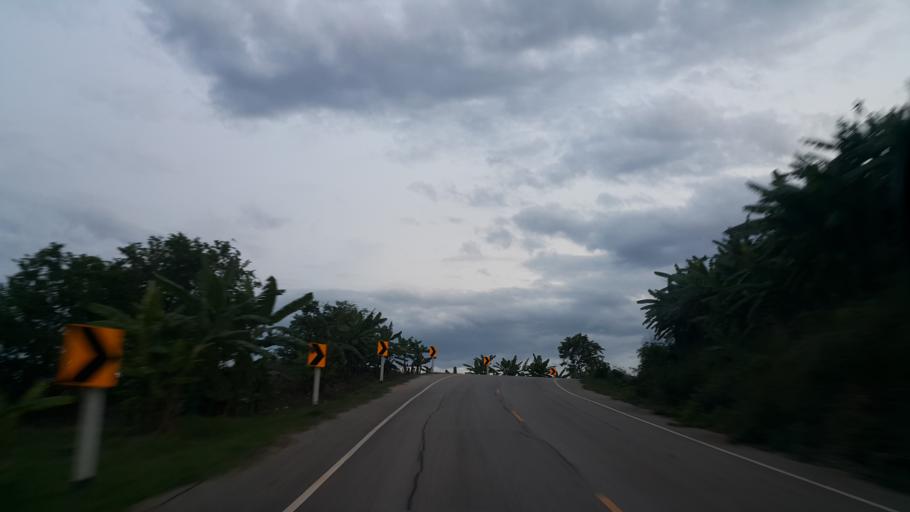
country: TH
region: Loei
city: Phu Ruea
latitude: 17.5244
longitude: 101.2324
